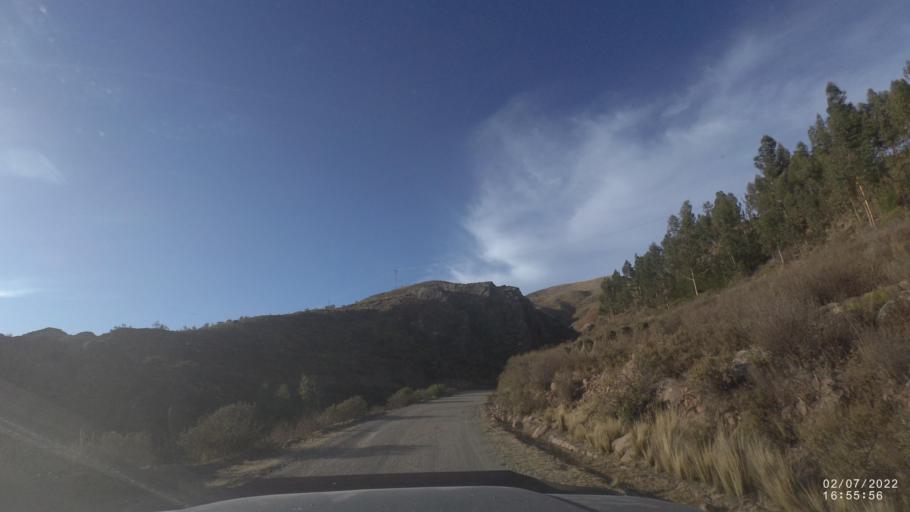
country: BO
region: Cochabamba
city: Irpa Irpa
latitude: -17.9571
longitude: -66.5434
